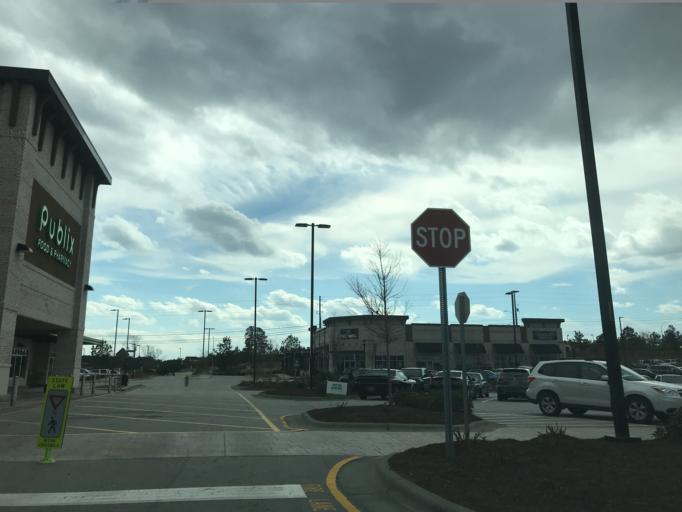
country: US
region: North Carolina
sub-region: Wake County
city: Morrisville
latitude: 35.7933
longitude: -78.8453
